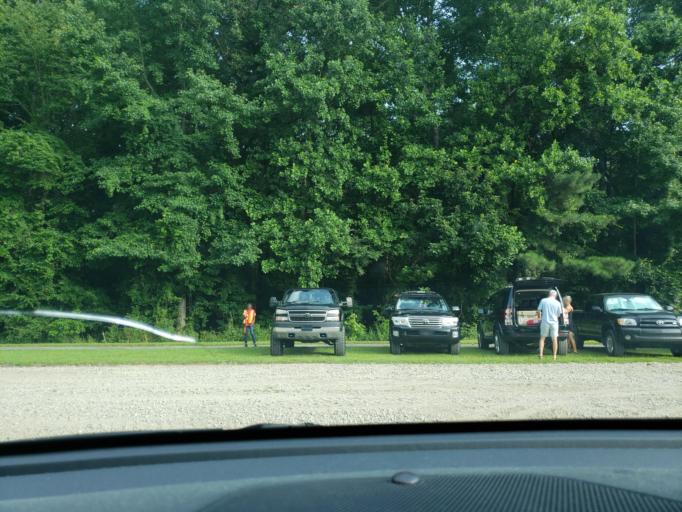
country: US
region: North Carolina
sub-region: Wake County
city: Garner
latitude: 35.7533
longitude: -78.5791
